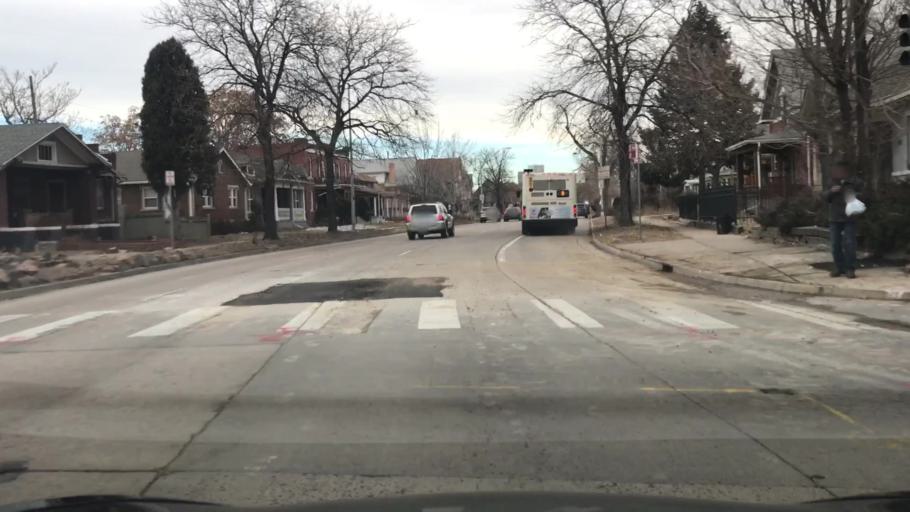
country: US
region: Colorado
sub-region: Denver County
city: Denver
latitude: 39.7075
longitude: -104.9863
